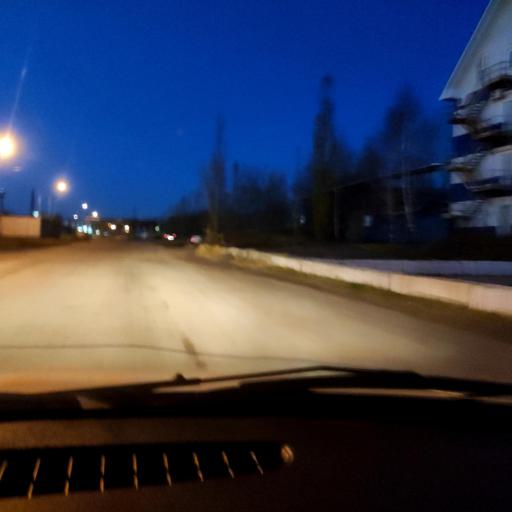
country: RU
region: Bashkortostan
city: Ufa
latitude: 54.8445
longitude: 56.0822
